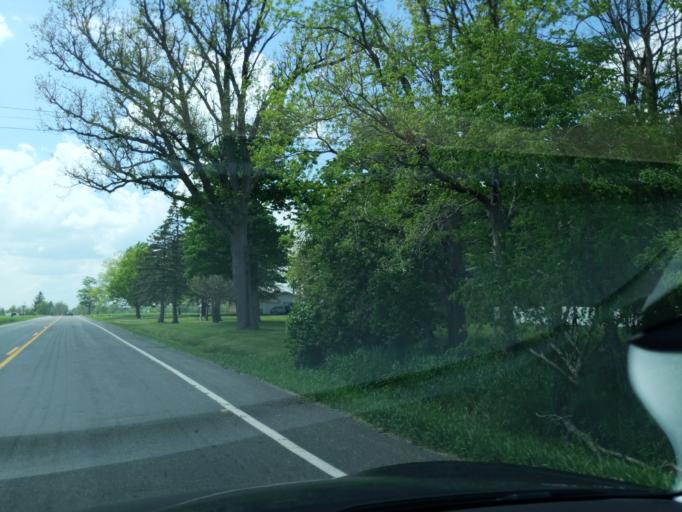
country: US
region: Michigan
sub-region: Ingham County
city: Mason
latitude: 42.5963
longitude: -84.3785
